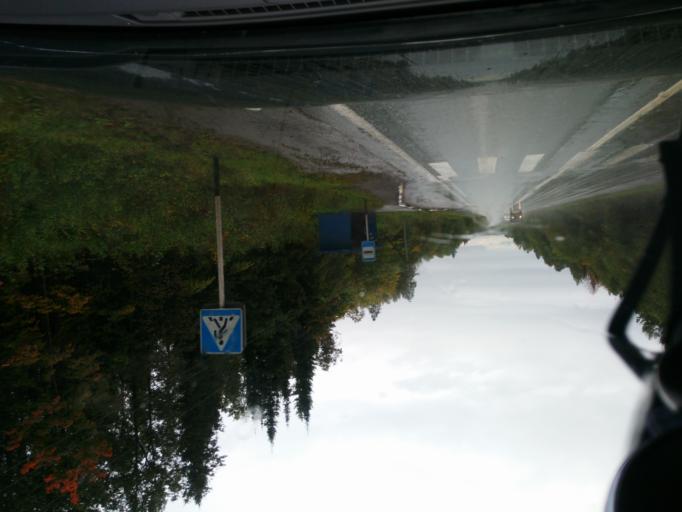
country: RU
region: Perm
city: Kultayevo
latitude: 57.8166
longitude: 55.7973
